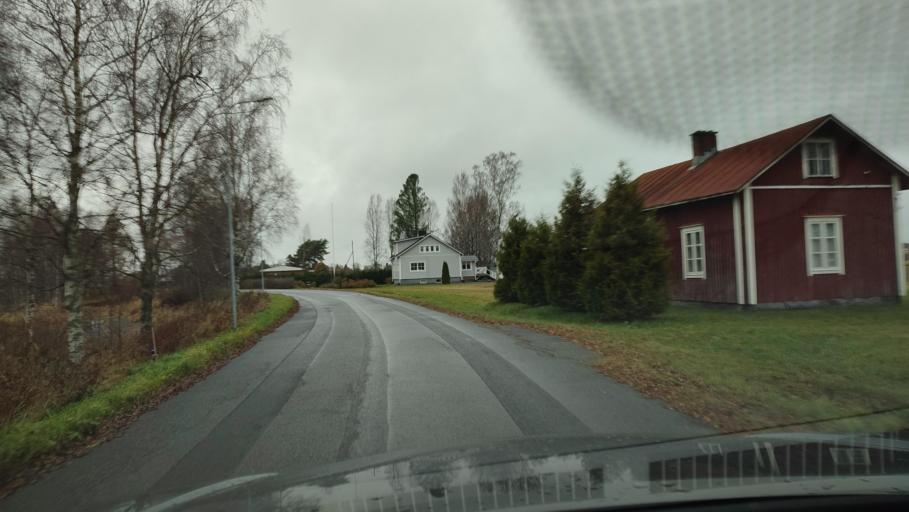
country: FI
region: Ostrobothnia
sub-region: Sydosterbotten
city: Kristinestad
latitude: 62.2536
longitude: 21.5407
